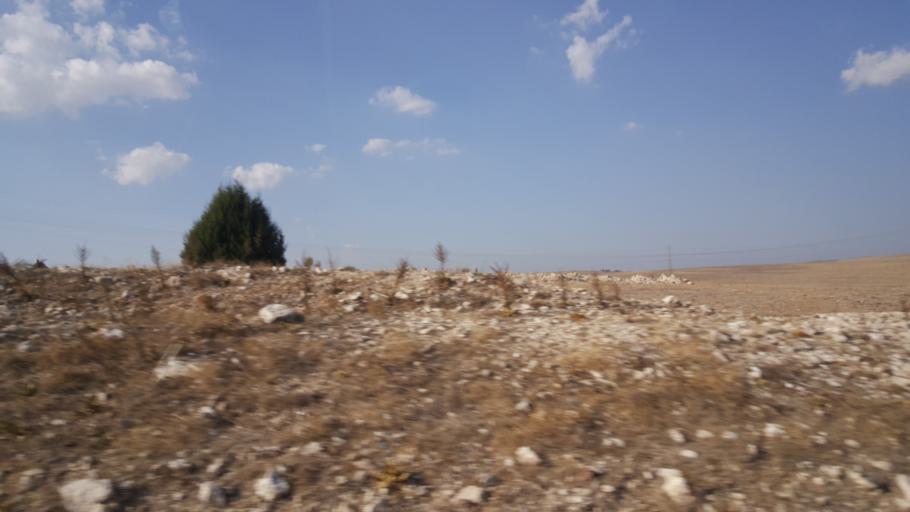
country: TR
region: Eskisehir
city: Kirka
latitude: 39.3206
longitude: 30.5553
